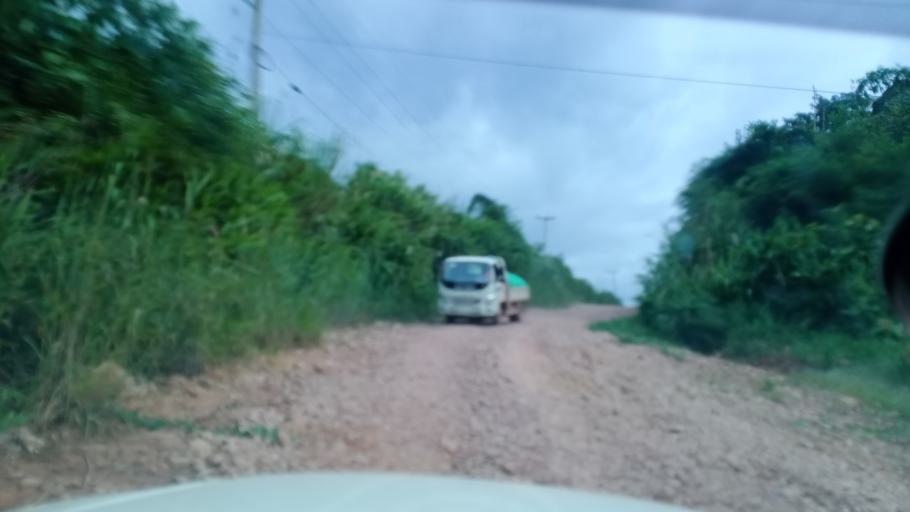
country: TH
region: Changwat Bueng Kan
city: Pak Khat
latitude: 18.7263
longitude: 103.2661
